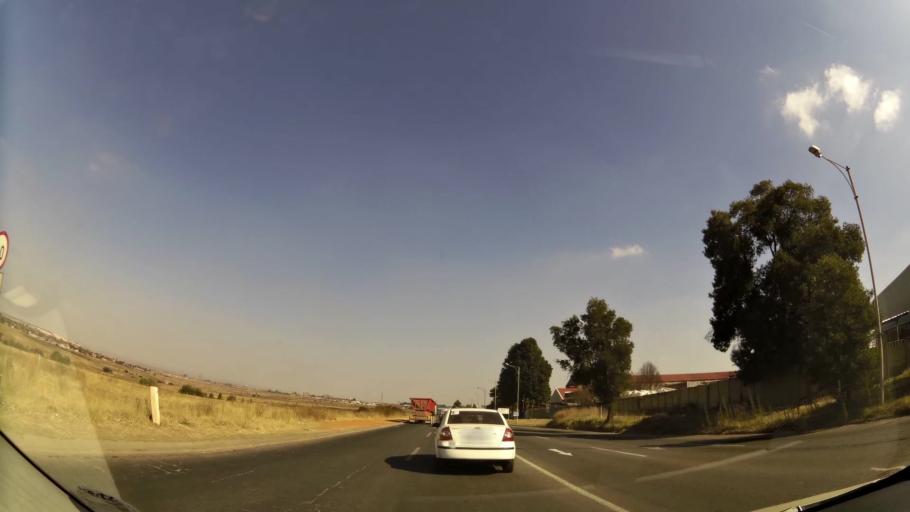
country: ZA
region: Gauteng
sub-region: City of Johannesburg Metropolitan Municipality
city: Roodepoort
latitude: -26.1482
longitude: 27.8128
